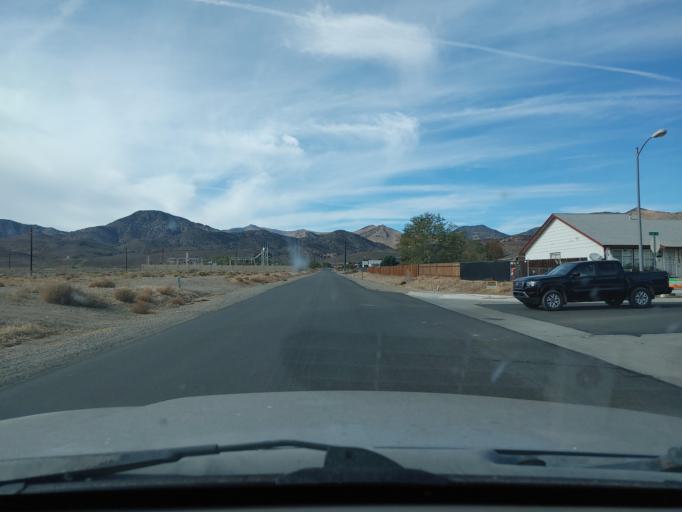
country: US
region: Nevada
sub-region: Lyon County
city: Dayton
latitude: 39.3029
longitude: -119.5428
